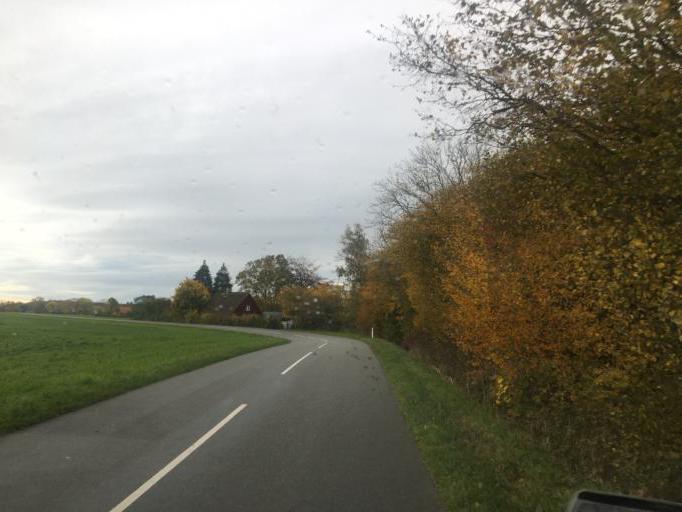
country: DK
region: Zealand
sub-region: Koge Kommune
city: Bjaeverskov
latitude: 55.4149
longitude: 11.9831
